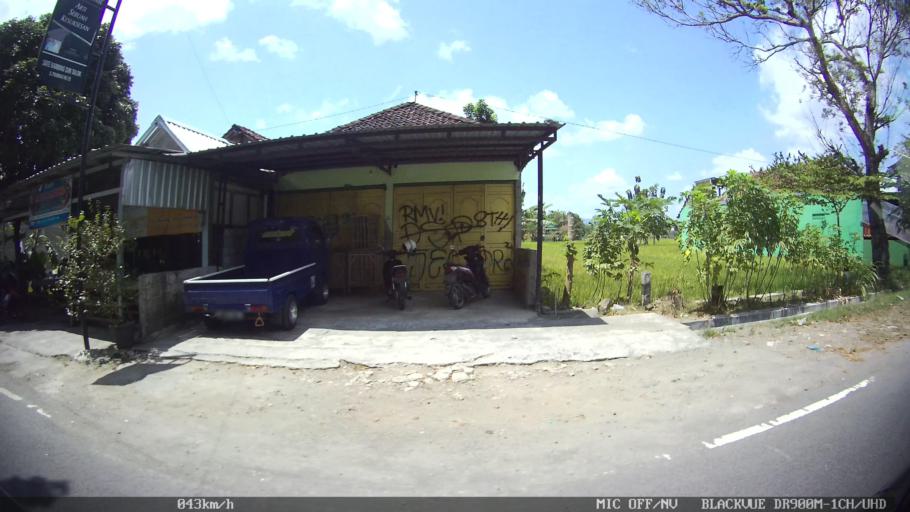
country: ID
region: Daerah Istimewa Yogyakarta
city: Sewon
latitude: -7.8892
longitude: 110.3475
